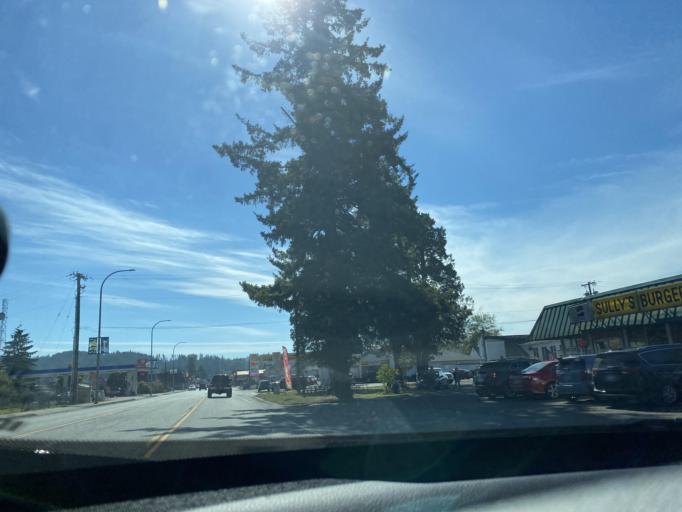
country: US
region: Washington
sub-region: Clallam County
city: Forks
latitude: 47.9536
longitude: -124.3854
